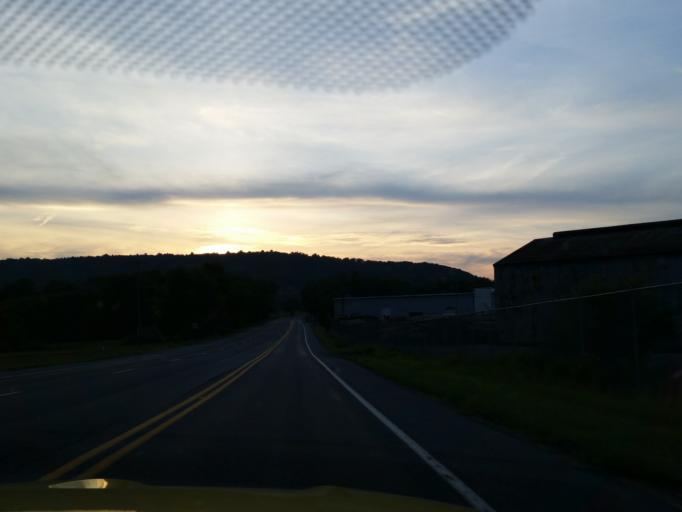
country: US
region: Pennsylvania
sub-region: Lebanon County
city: Jonestown
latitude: 40.4260
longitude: -76.5851
